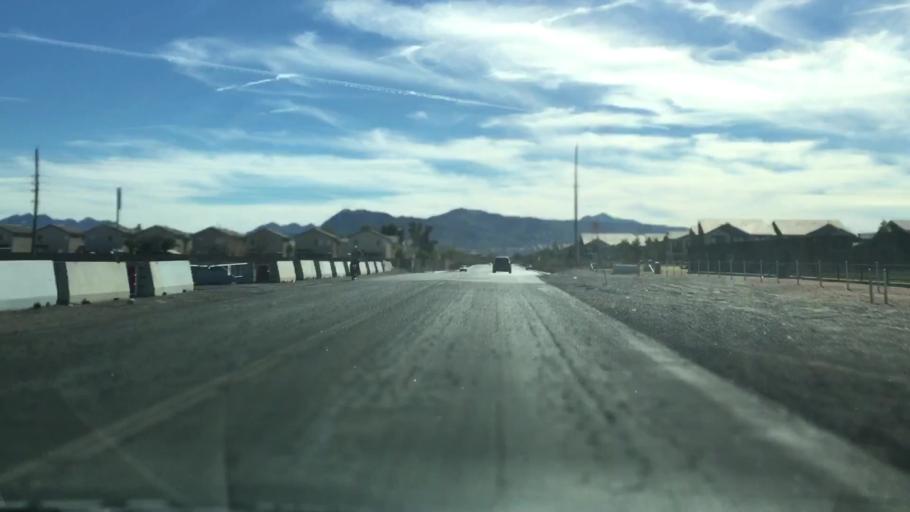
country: US
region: Nevada
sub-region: Clark County
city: Henderson
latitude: 36.0833
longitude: -115.0205
